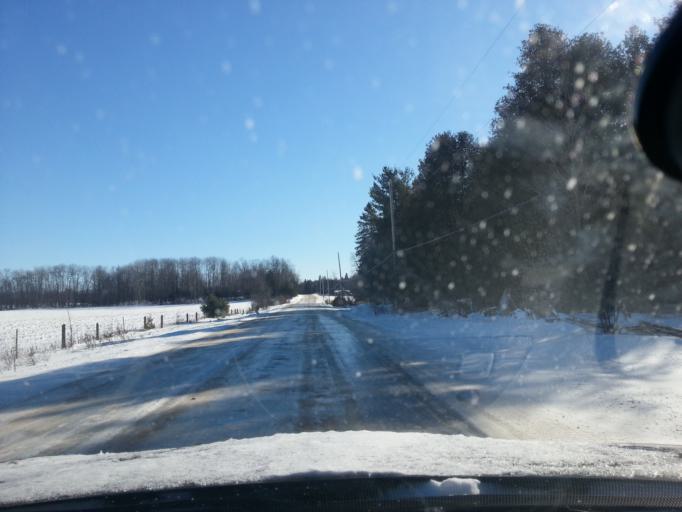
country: CA
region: Ontario
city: Arnprior
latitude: 45.2534
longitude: -76.3152
